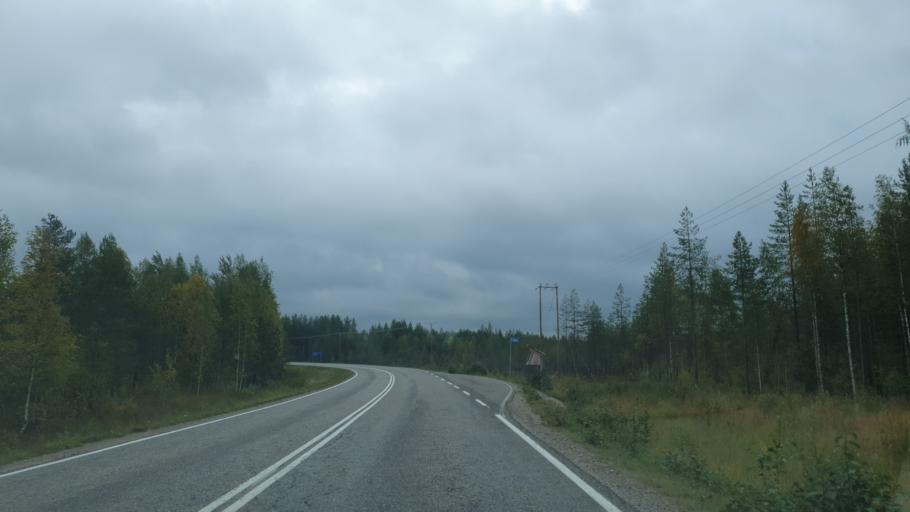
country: FI
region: Kainuu
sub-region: Kehys-Kainuu
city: Kuhmo
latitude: 64.2261
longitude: 29.8114
